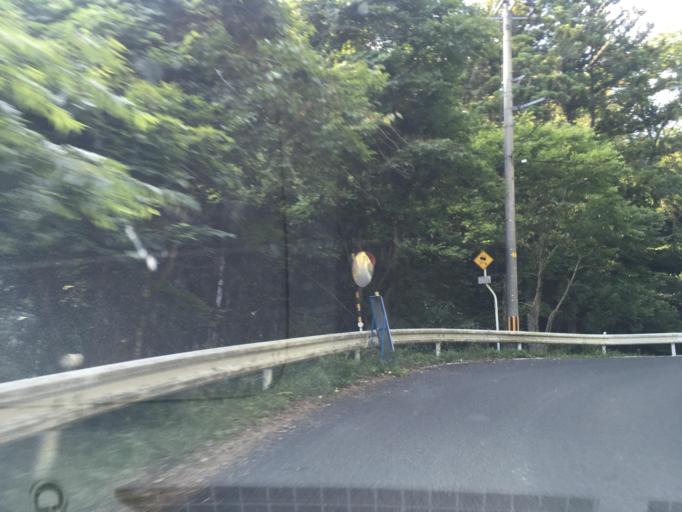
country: JP
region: Iwate
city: Ofunato
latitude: 38.9135
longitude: 141.6186
